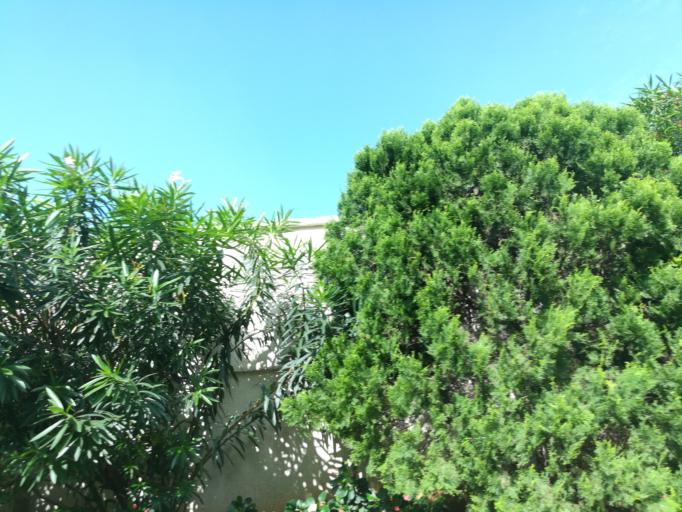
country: NG
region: Lagos
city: Ojota
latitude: 6.5765
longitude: 3.3636
